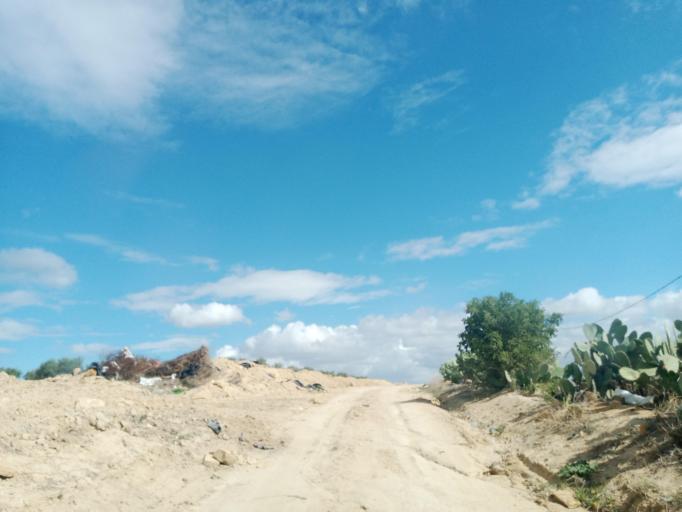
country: TN
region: Tunis
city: Oued Lill
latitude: 36.8091
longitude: 9.9890
